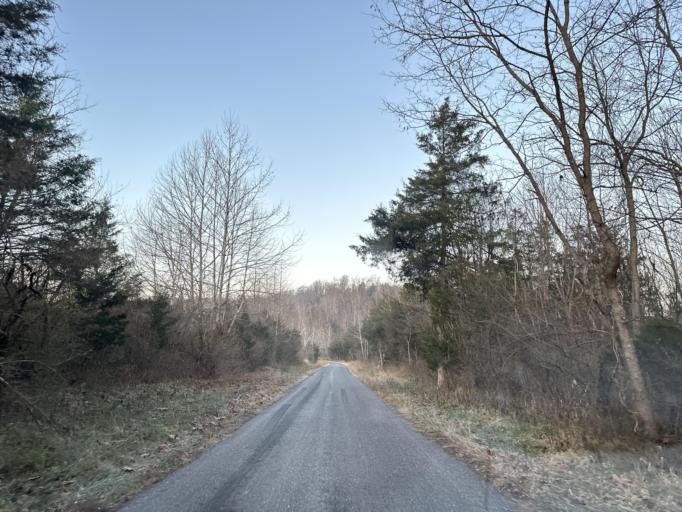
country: US
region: Virginia
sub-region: Rockbridge County
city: East Lexington
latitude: 38.0755
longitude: -79.3720
